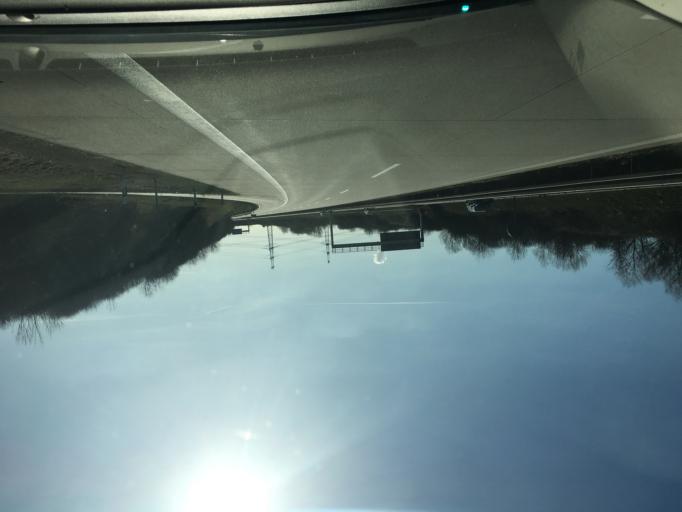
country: DE
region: Saxony
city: Hartmannsdorf
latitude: 50.8672
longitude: 12.8065
